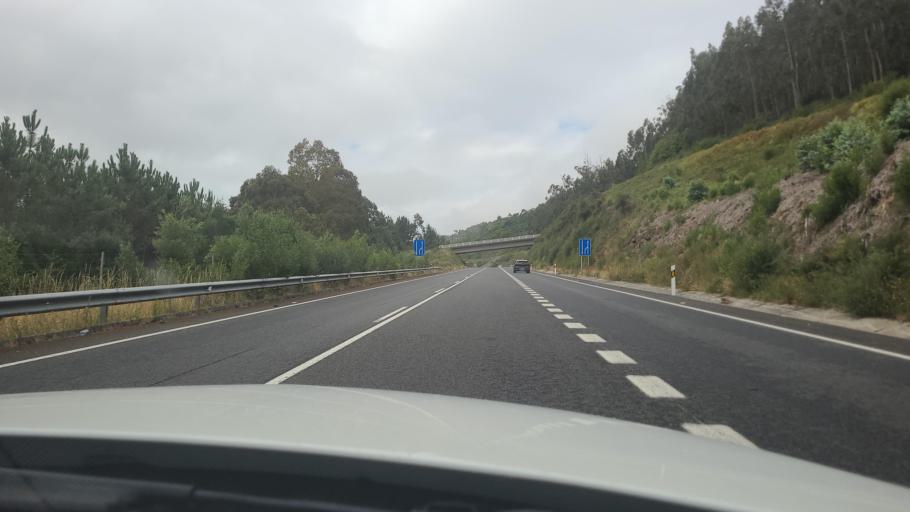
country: ES
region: Galicia
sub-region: Provincia da Coruna
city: Cee
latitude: 42.9675
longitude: -9.2042
